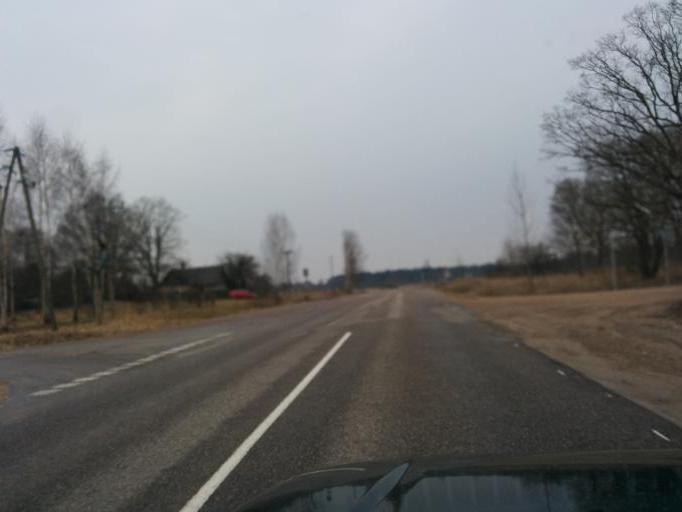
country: LV
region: Ikskile
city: Ikskile
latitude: 56.8203
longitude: 24.4489
